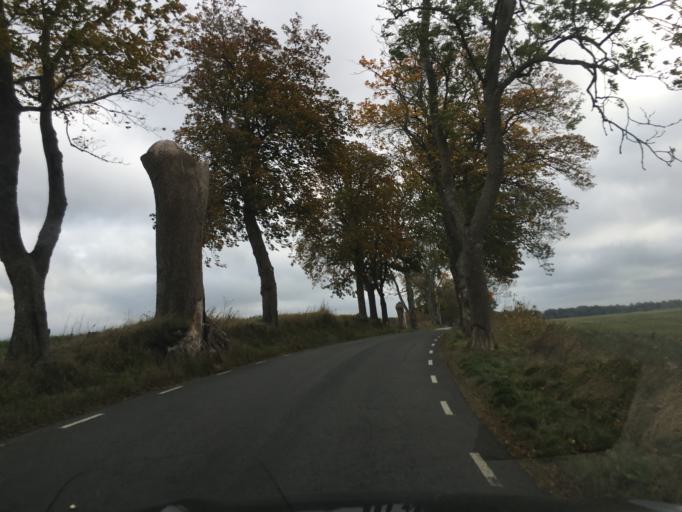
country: SE
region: Skane
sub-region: Tomelilla Kommun
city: Tomelilla
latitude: 55.6512
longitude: 14.0336
